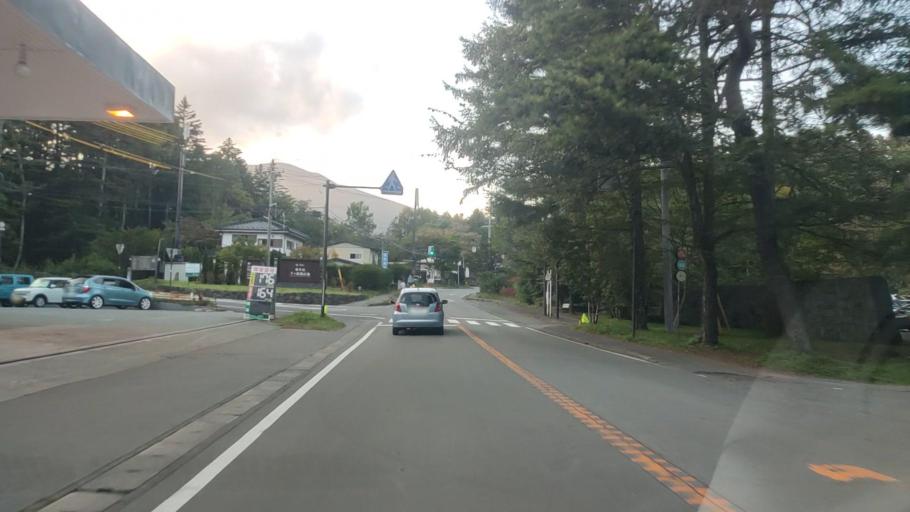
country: JP
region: Nagano
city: Komoro
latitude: 36.3612
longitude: 138.5885
